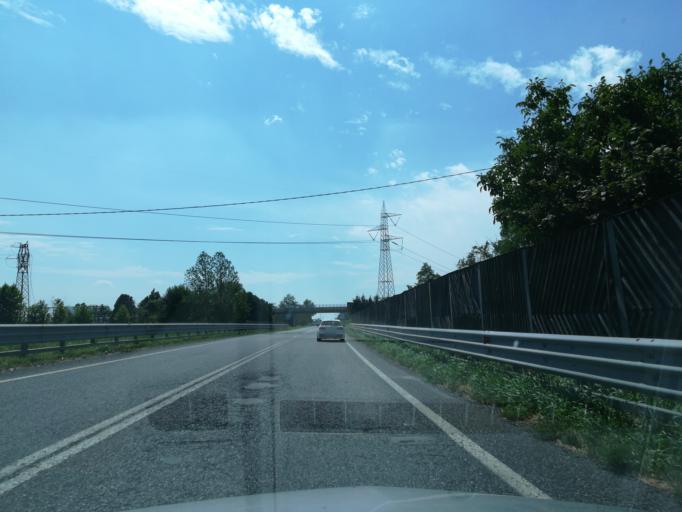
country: IT
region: Lombardy
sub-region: Provincia di Bergamo
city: Grassobbio
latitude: 45.6419
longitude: 9.7256
